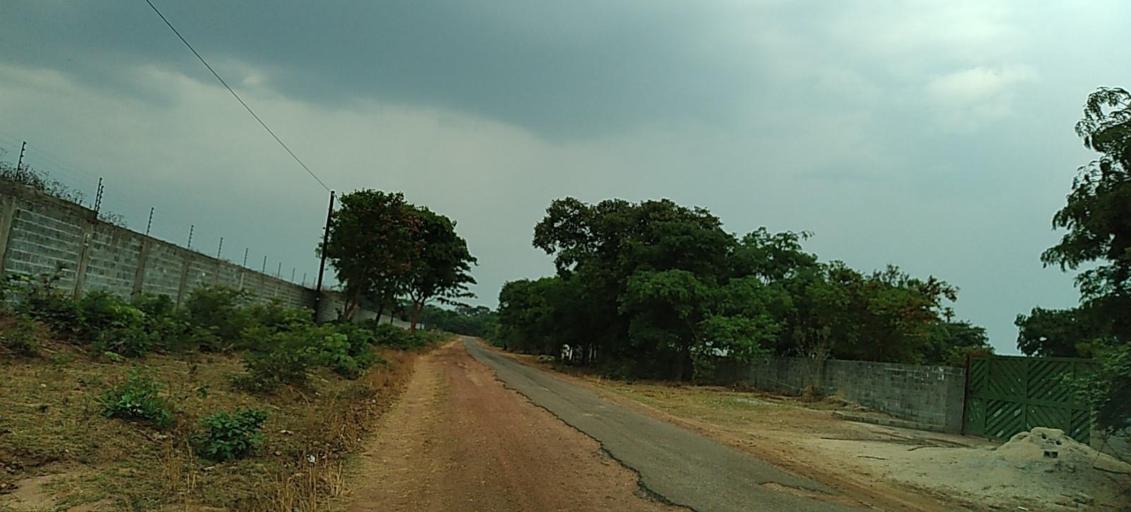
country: ZM
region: Copperbelt
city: Kalulushi
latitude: -12.8890
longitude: 28.1222
